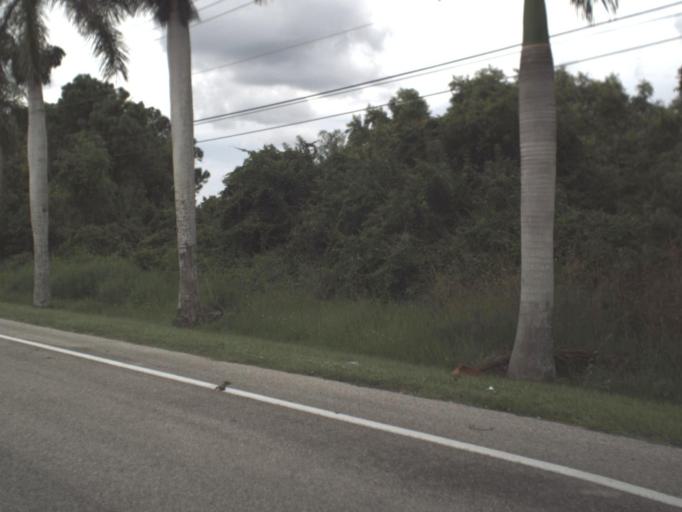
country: US
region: Florida
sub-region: Lee County
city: Tice
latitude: 26.6925
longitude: -81.7842
